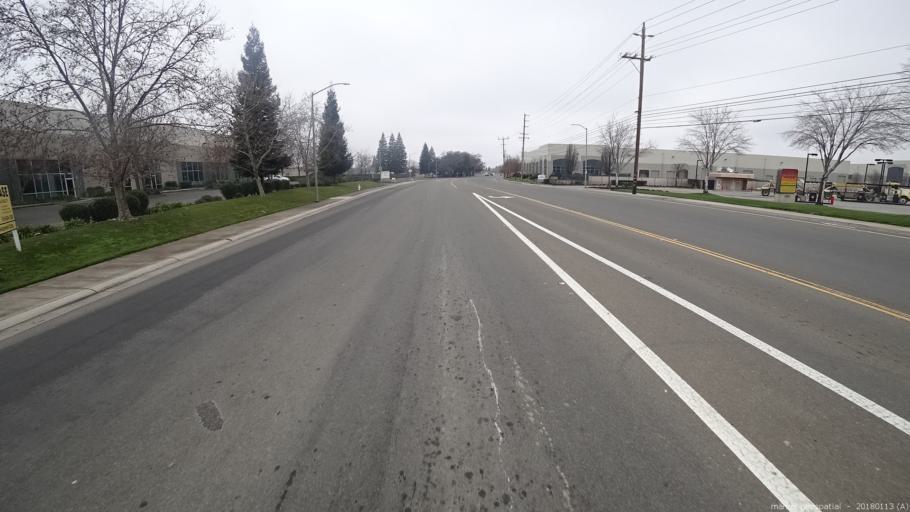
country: US
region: California
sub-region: Sacramento County
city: Gold River
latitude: 38.5902
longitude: -121.2600
